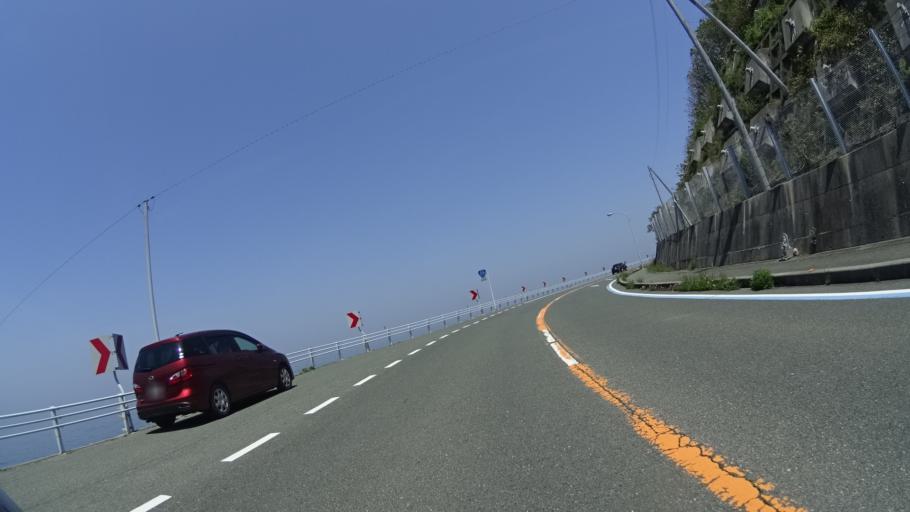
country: JP
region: Ehime
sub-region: Nishiuwa-gun
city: Ikata-cho
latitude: 33.5753
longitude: 132.4419
